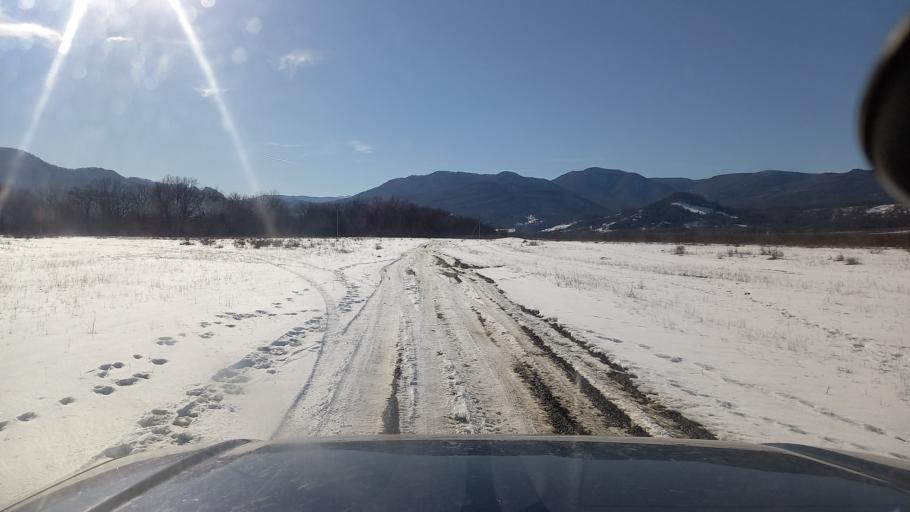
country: RU
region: Adygeya
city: Kamennomostskiy
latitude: 44.2199
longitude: 40.1809
